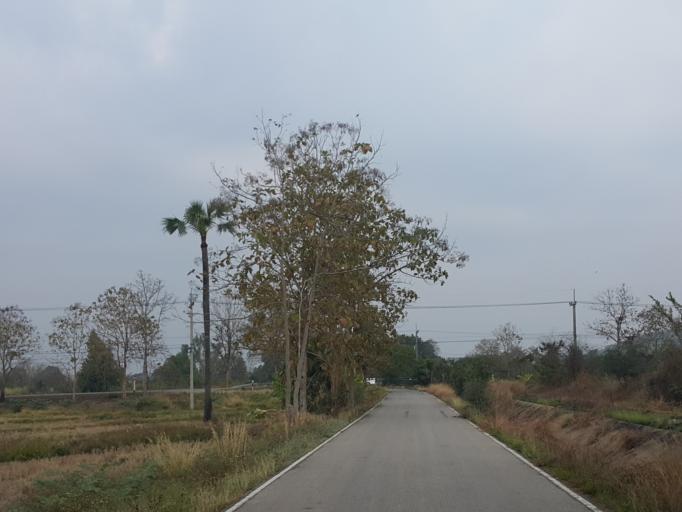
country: TH
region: Chiang Mai
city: San Kamphaeng
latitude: 18.7292
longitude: 99.1913
